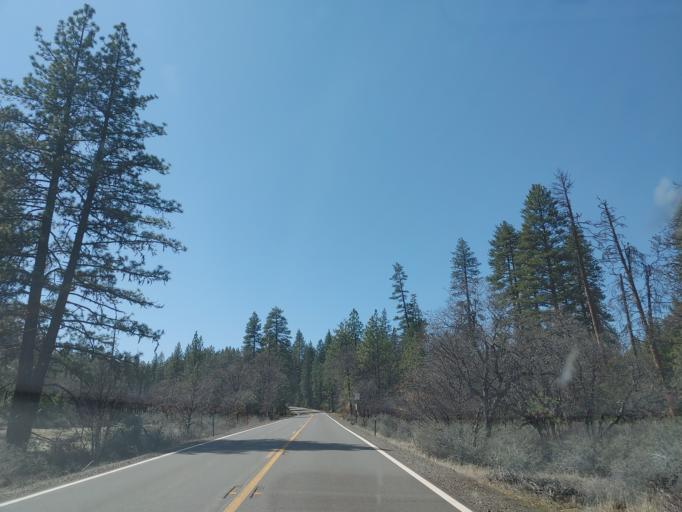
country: US
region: California
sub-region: Shasta County
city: Burney
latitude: 41.0157
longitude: -121.6437
